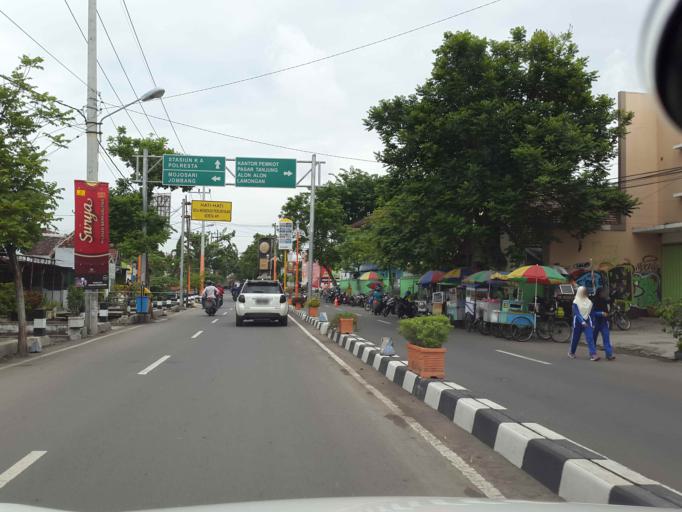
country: ID
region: East Java
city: Mojokerto
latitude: -7.4720
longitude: 112.4412
